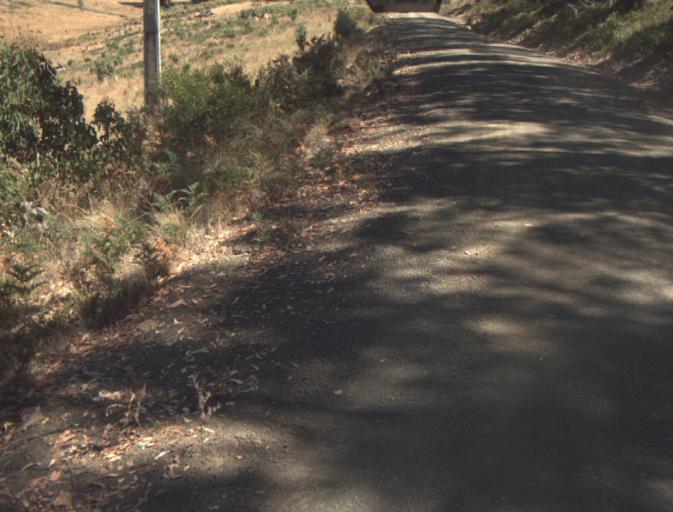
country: AU
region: Tasmania
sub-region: Dorset
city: Scottsdale
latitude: -41.3512
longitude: 147.3859
